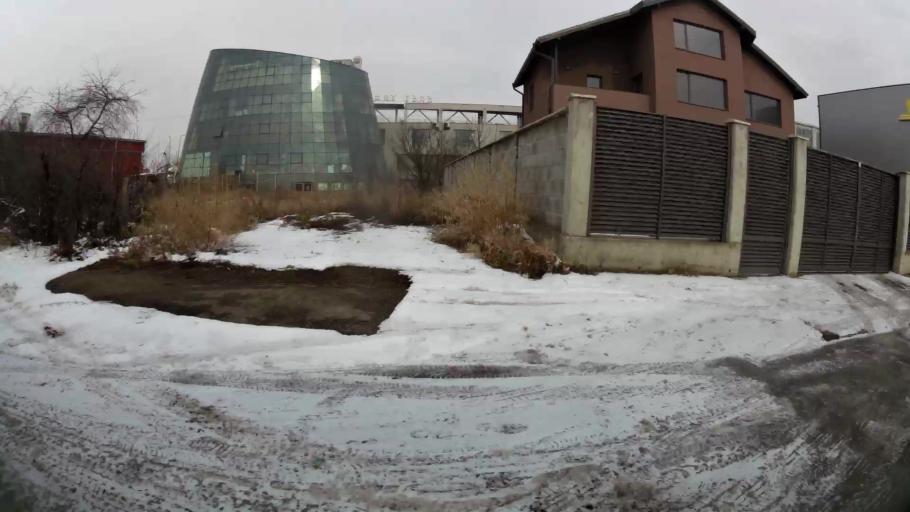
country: BG
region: Sofia-Capital
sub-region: Stolichna Obshtina
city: Sofia
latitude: 42.7068
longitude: 23.4116
